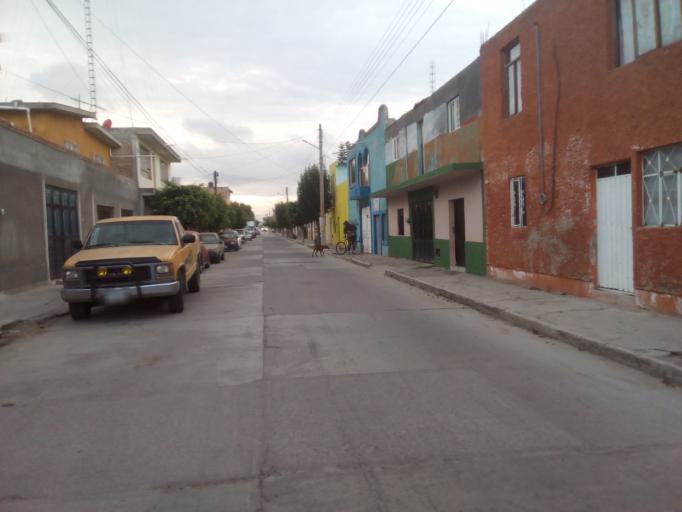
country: MX
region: Guanajuato
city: San Jose Iturbide
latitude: 21.0064
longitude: -100.3873
